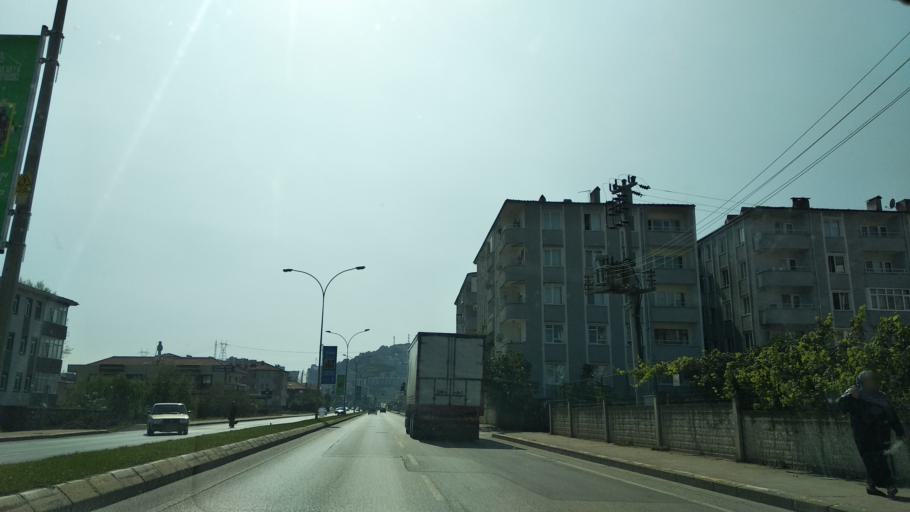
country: TR
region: Sakarya
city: Adapazari
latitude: 40.7652
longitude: 30.3635
